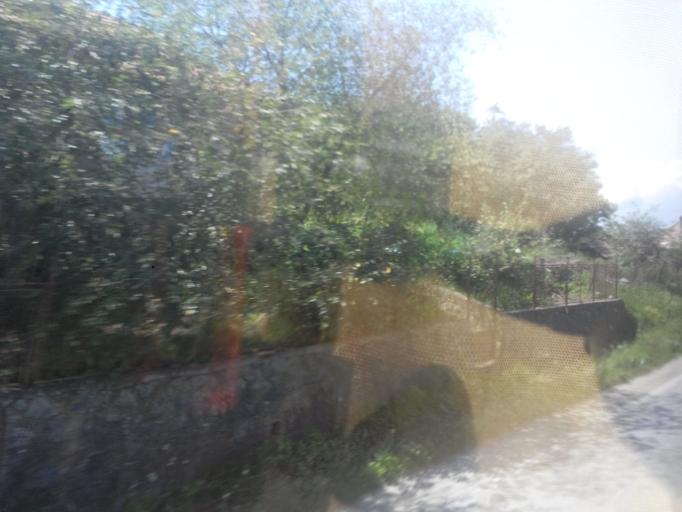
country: RO
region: Hunedoara
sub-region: Comuna Dobra
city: Dobra
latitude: 45.9104
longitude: 22.5747
